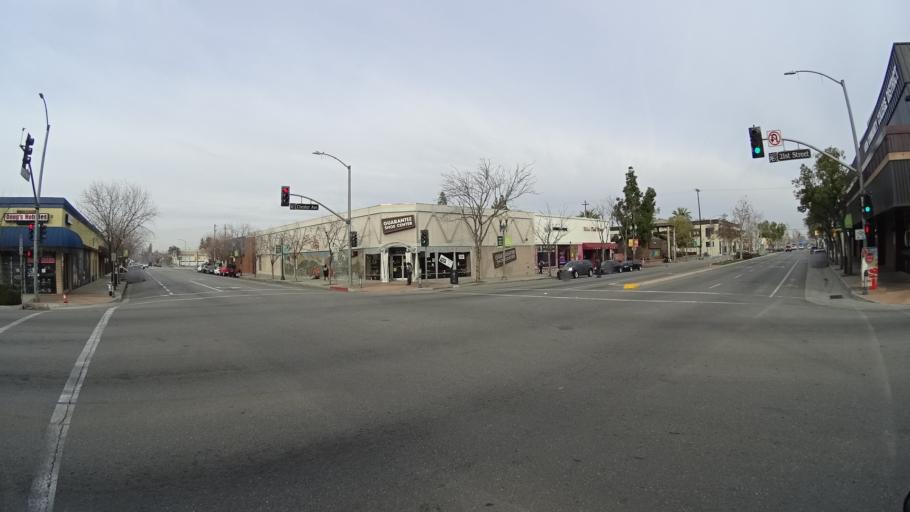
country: US
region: California
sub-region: Kern County
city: Bakersfield
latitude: 35.3780
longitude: -119.0187
